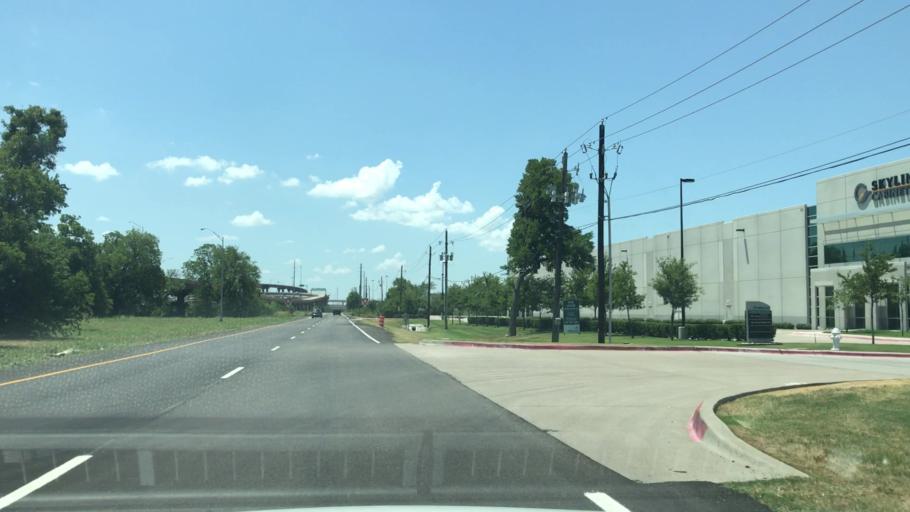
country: US
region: Texas
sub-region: Dallas County
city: Farmers Branch
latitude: 32.9183
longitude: -96.9003
